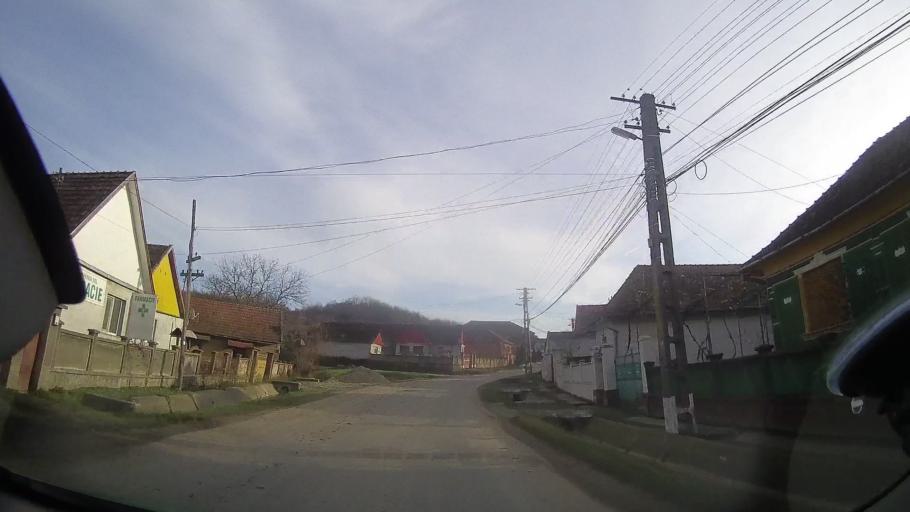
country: RO
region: Bihor
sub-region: Comuna Sarbi
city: Burzuc
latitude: 47.1556
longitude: 22.1691
